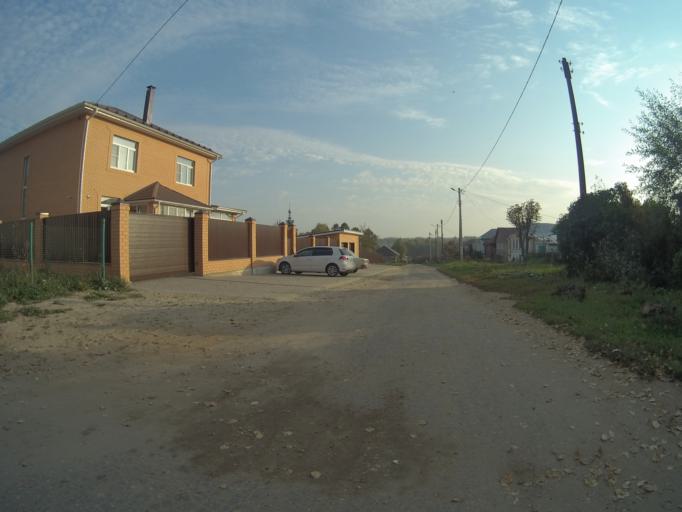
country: RU
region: Vladimir
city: Bogolyubovo
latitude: 56.1917
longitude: 40.4915
